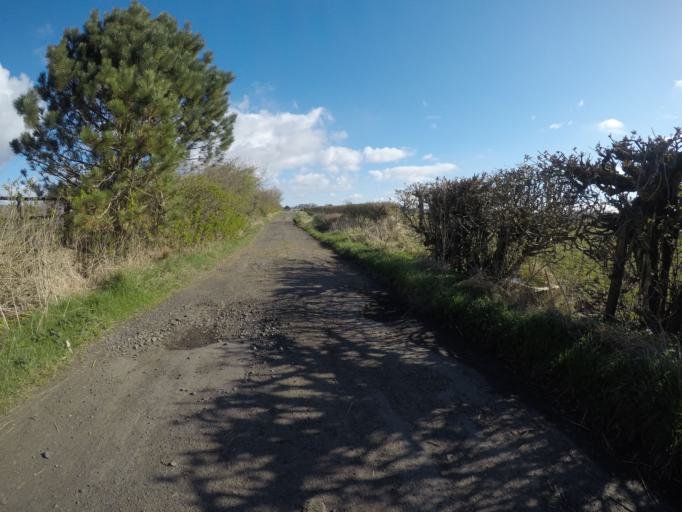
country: GB
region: Scotland
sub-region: North Ayrshire
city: Irvine
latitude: 55.6510
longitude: -4.6579
